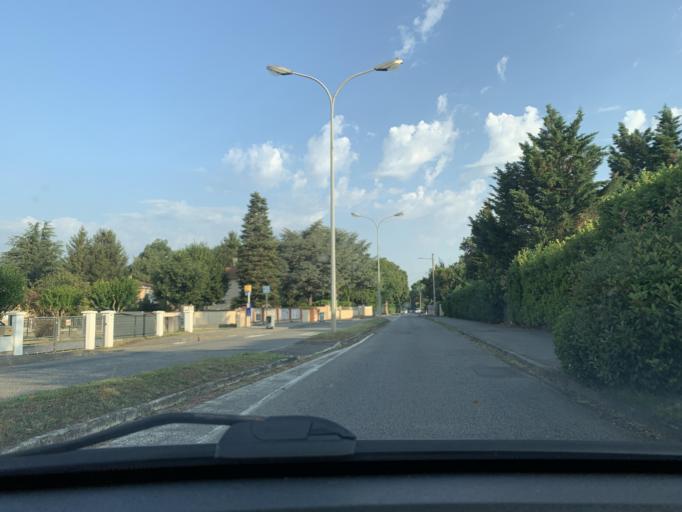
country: FR
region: Midi-Pyrenees
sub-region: Departement de la Haute-Garonne
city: Labege
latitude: 43.5323
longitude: 1.5339
